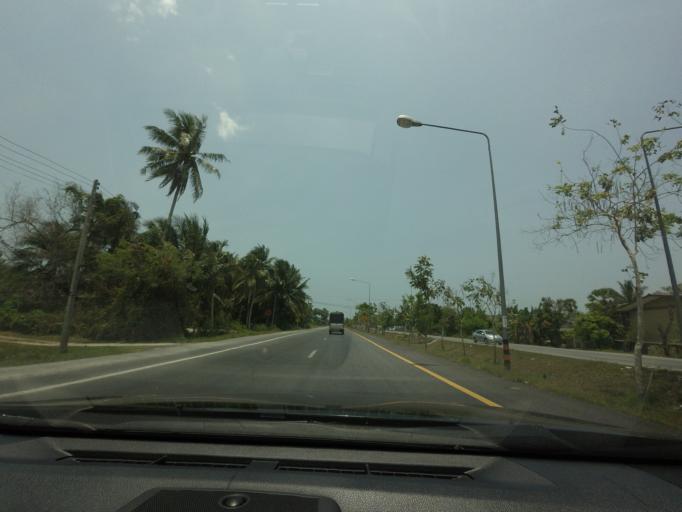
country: TH
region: Pattani
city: Pattani
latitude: 6.8502
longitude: 101.2235
